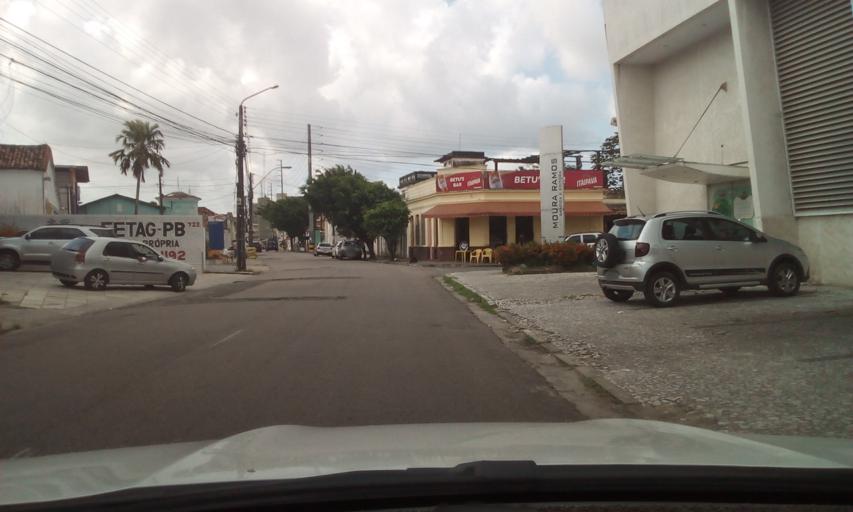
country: BR
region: Paraiba
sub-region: Joao Pessoa
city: Joao Pessoa
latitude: -7.1288
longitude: -34.8827
